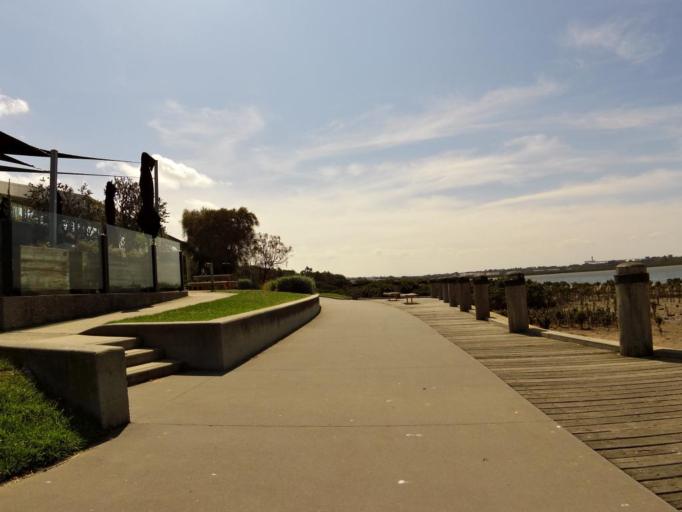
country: AU
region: Victoria
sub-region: Mornington Peninsula
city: Hastings
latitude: -38.3084
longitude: 145.1977
